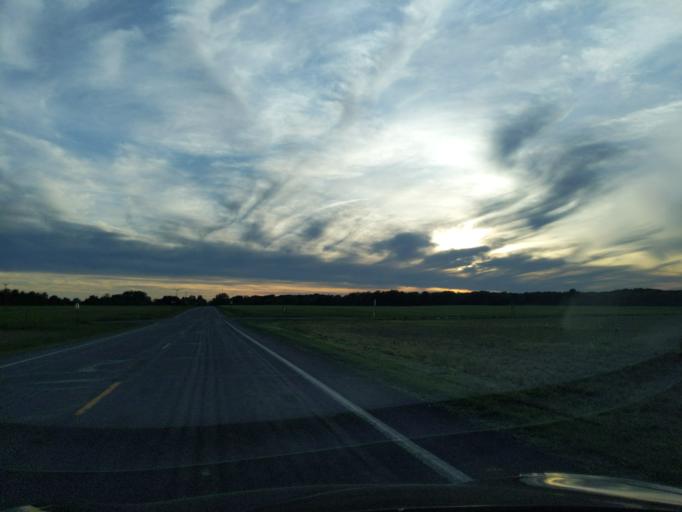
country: US
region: Michigan
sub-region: Ingham County
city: Williamston
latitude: 42.6009
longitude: -84.3175
